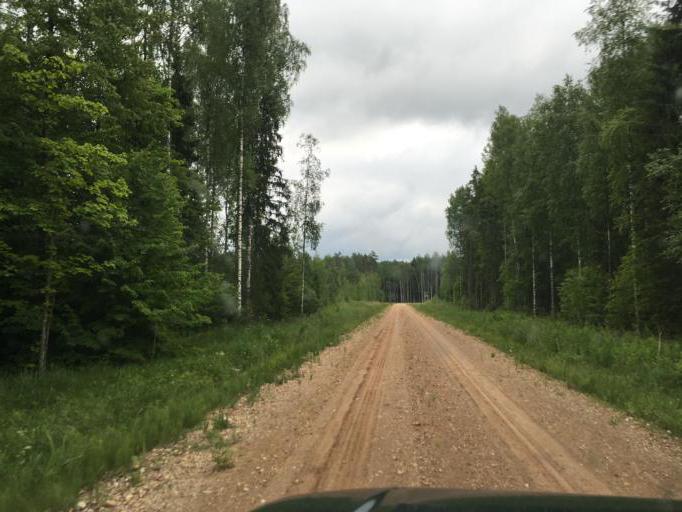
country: LV
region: Vilaka
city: Vilaka
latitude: 57.3885
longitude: 27.4906
